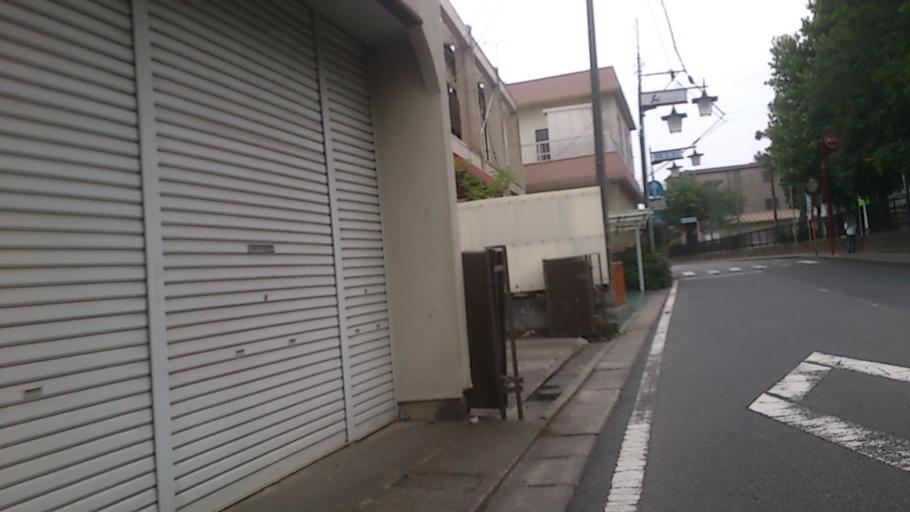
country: JP
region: Ibaraki
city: Mito-shi
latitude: 36.3724
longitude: 140.4395
